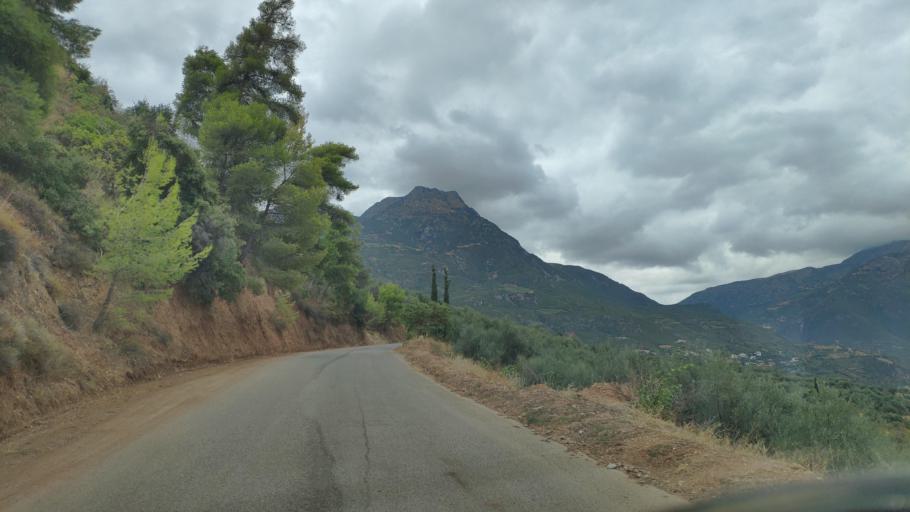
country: GR
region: West Greece
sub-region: Nomos Achaias
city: Temeni
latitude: 38.1752
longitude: 22.1436
